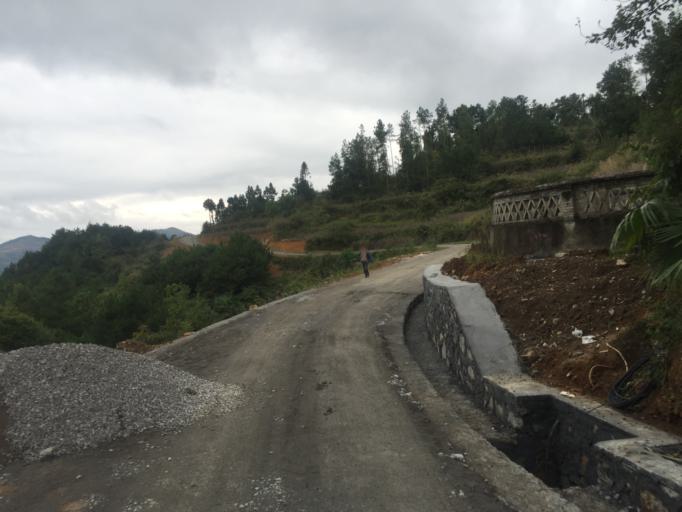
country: CN
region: Guizhou Sheng
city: Chaodi
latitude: 27.9852
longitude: 108.2193
